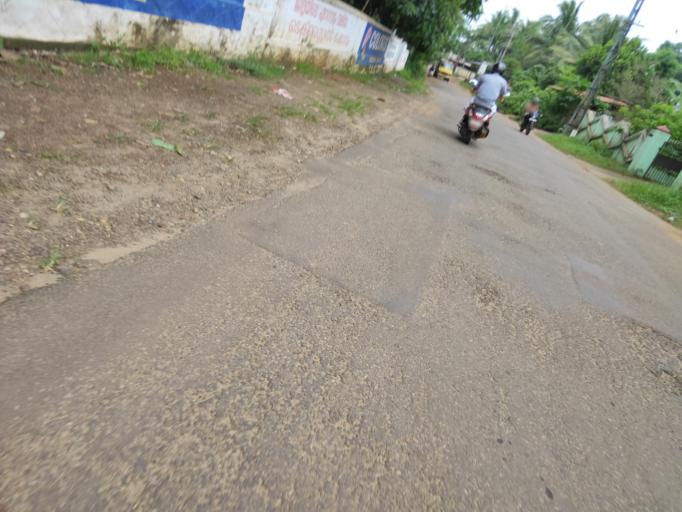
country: IN
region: Kerala
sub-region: Malappuram
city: Manjeri
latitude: 11.2437
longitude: 76.2873
